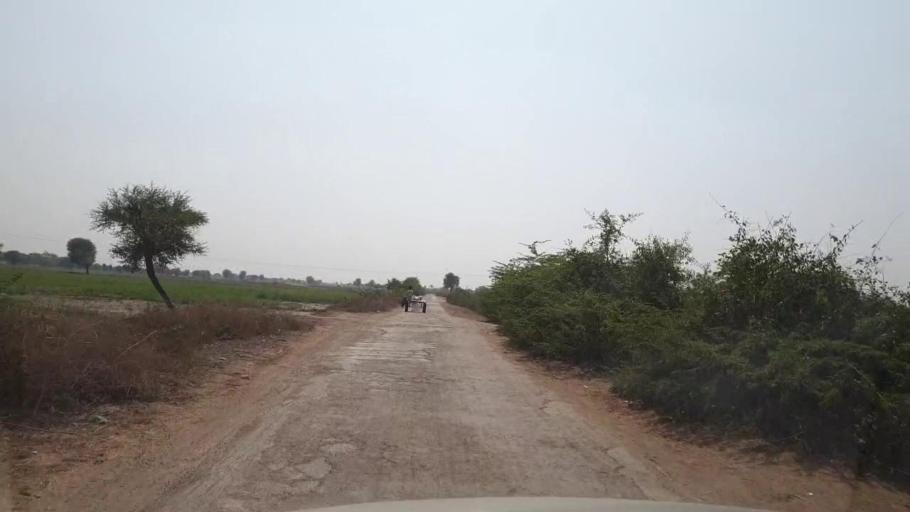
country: PK
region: Sindh
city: Dhoro Naro
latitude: 25.4735
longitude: 69.6384
